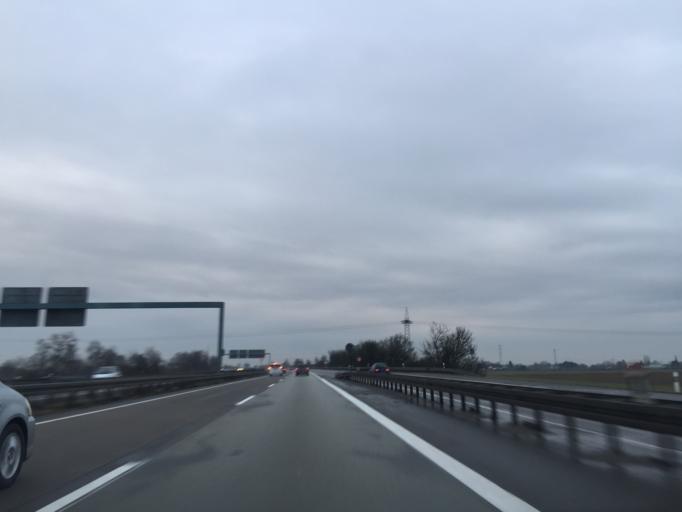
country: DE
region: Hesse
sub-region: Regierungsbezirk Darmstadt
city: Hochheim am Main
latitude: 50.0528
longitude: 8.3902
